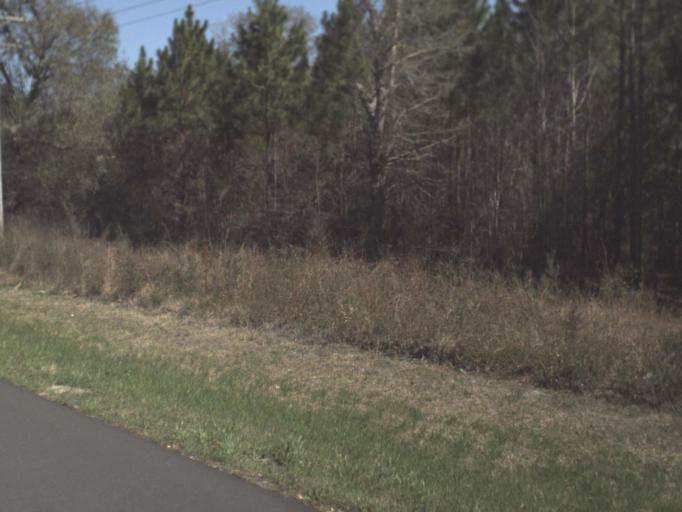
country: US
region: Florida
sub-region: Jackson County
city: Sneads
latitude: 30.7326
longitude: -85.0199
